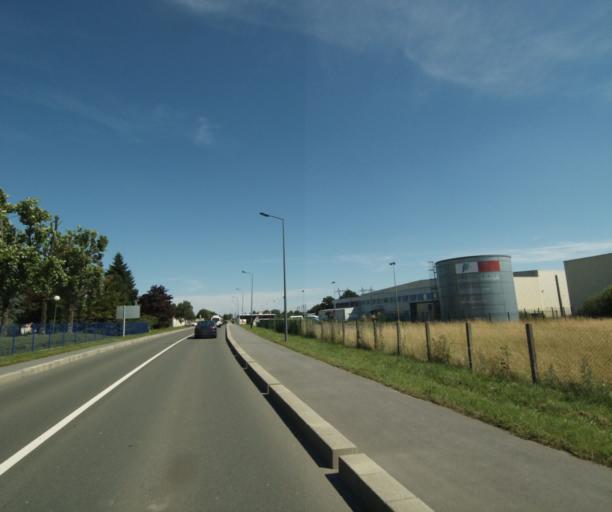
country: FR
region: Pays de la Loire
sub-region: Departement de la Mayenne
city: Laval
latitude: 48.0546
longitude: -0.7980
